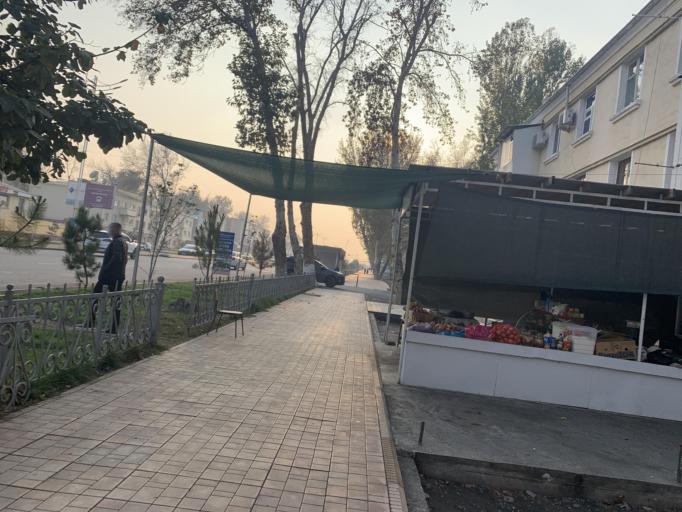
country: UZ
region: Fergana
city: Qo`qon
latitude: 40.5269
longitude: 70.9392
